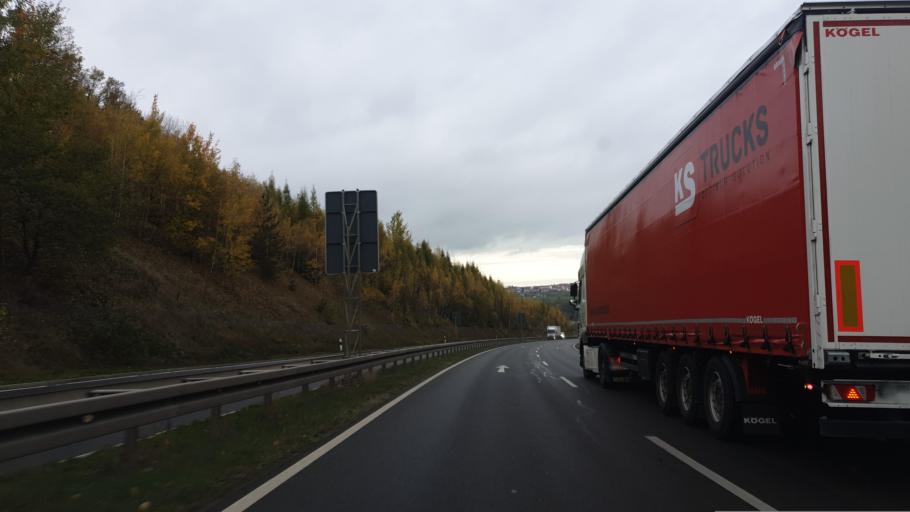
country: DE
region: Saxony
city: Reichenbach/Vogtland
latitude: 50.6051
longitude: 12.3165
